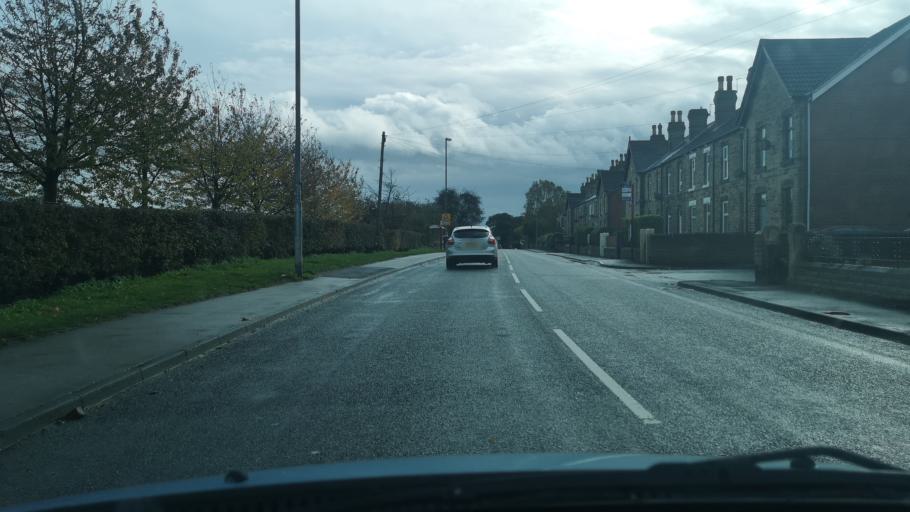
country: GB
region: England
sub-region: City and Borough of Wakefield
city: Hemsworth
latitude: 53.6173
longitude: -1.3553
